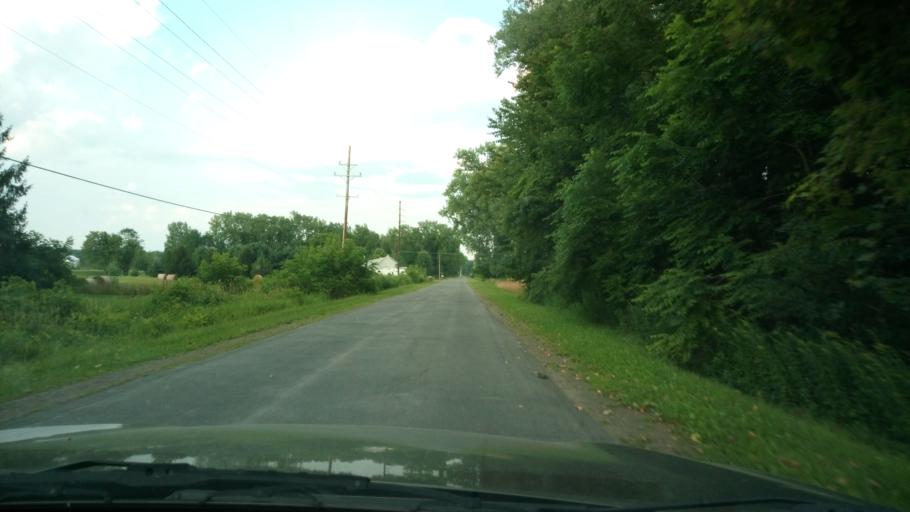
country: US
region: New York
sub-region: Wayne County
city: Clyde
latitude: 43.0886
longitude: -76.9035
